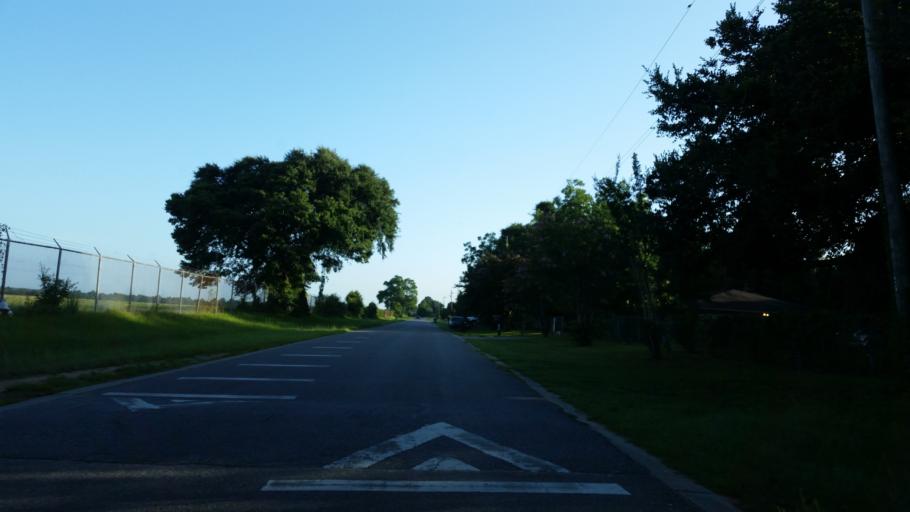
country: US
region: Florida
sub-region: Escambia County
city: Bellview
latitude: 30.4655
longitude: -87.3326
